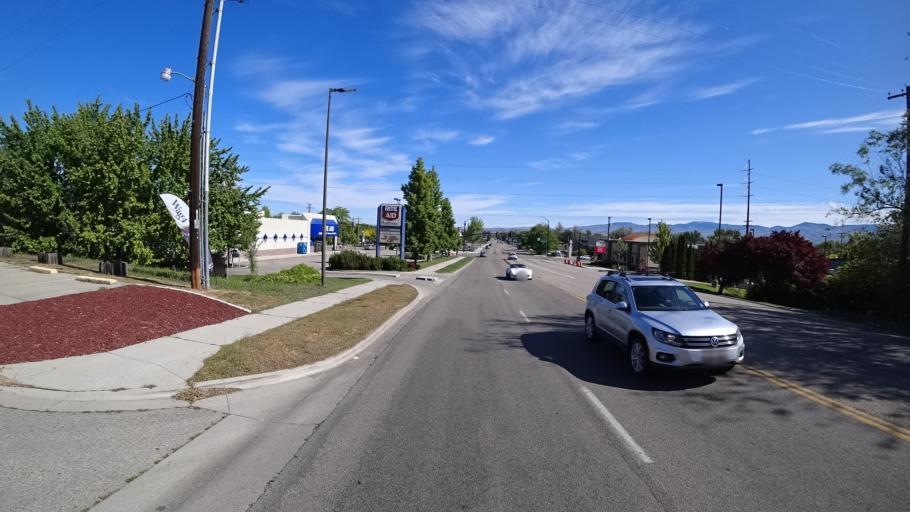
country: US
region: Idaho
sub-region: Ada County
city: Garden City
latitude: 43.5888
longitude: -116.2437
